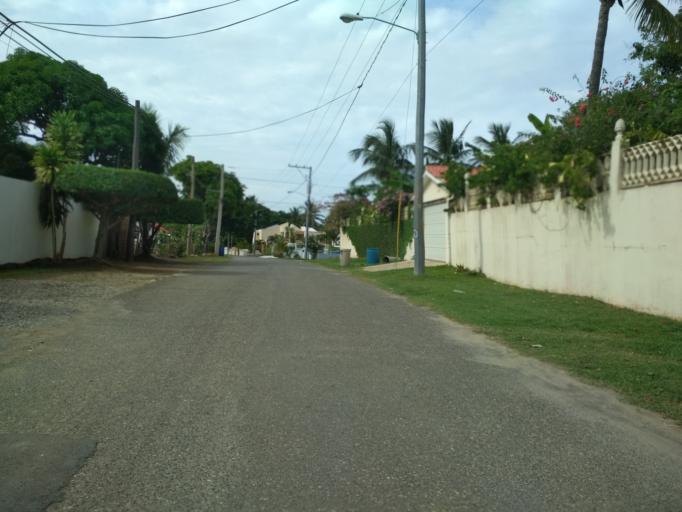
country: DO
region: Puerto Plata
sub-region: Puerto Plata
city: Puerto Plata
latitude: 19.8134
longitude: -70.7164
